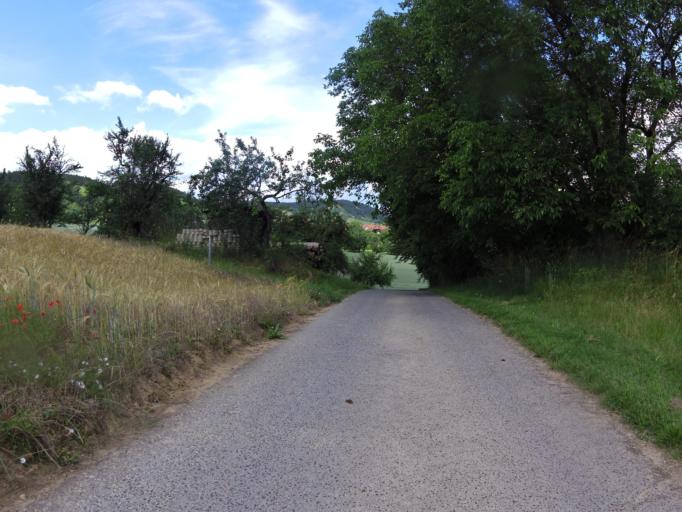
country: DE
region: Bavaria
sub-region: Regierungsbezirk Unterfranken
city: Erlabrunn
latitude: 49.8517
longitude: 9.8499
